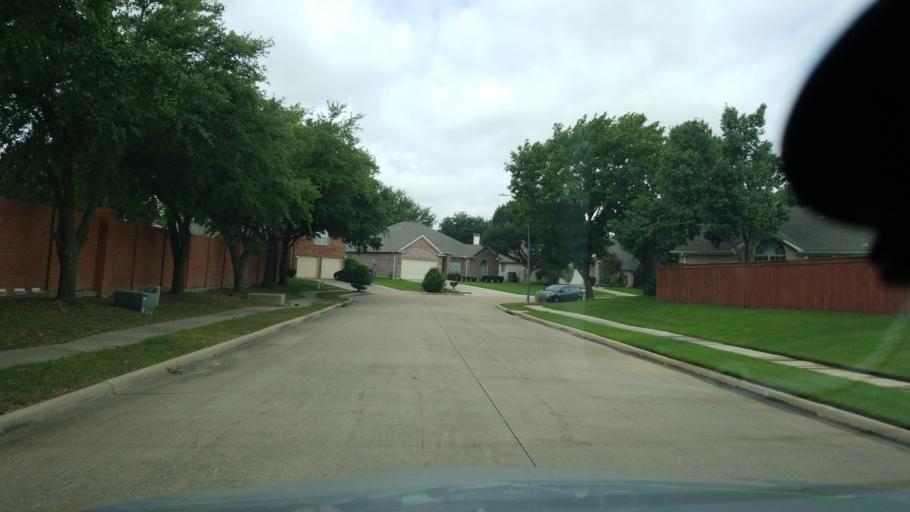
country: US
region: Texas
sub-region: Dallas County
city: Farmers Branch
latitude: 32.9439
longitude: -96.9455
